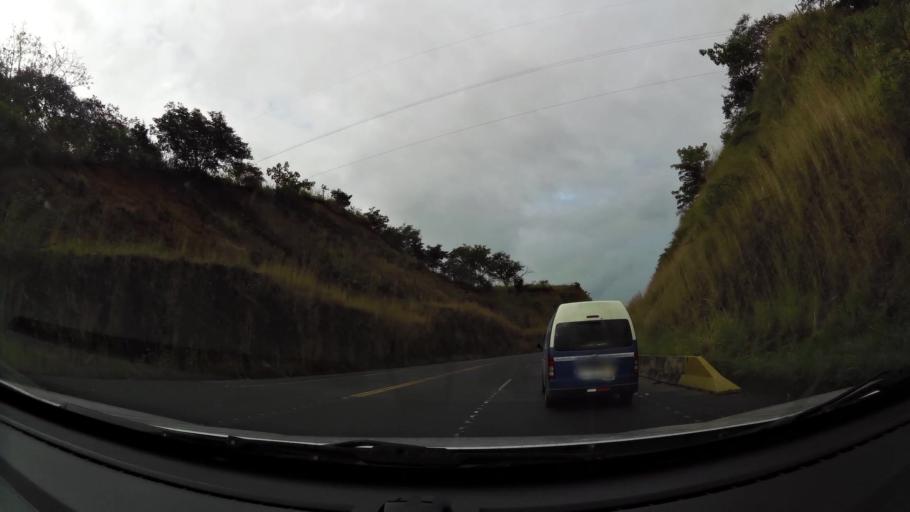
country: CR
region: Alajuela
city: Atenas
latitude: 9.9655
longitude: -84.3426
